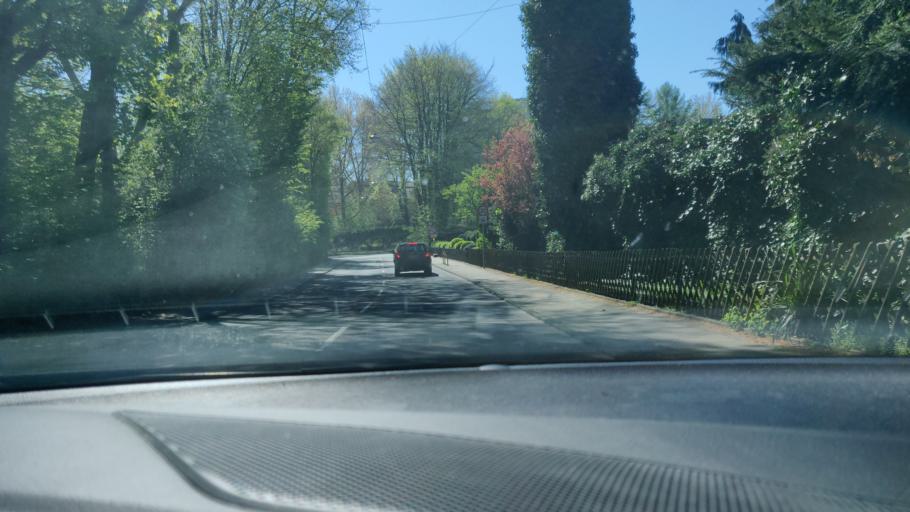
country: DE
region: North Rhine-Westphalia
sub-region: Regierungsbezirk Dusseldorf
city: Mettmann
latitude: 51.2506
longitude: 6.9683
